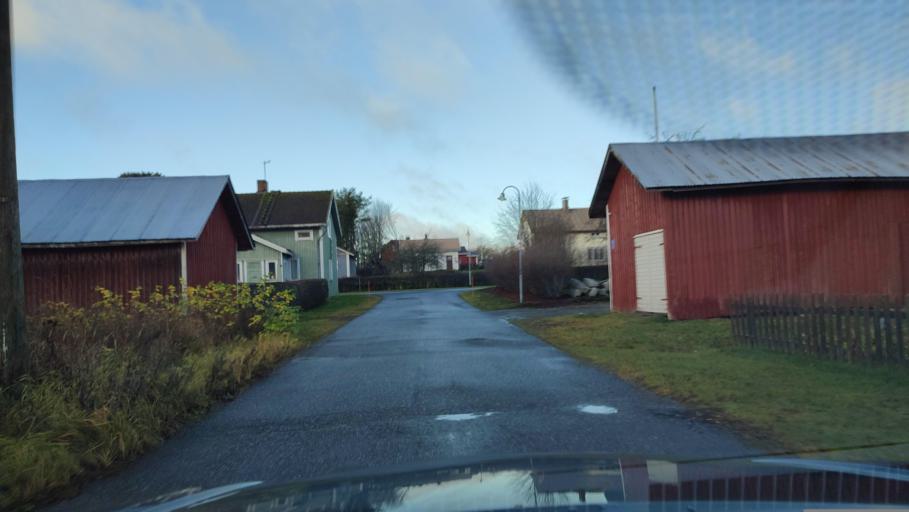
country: FI
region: Ostrobothnia
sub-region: Sydosterbotten
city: Kristinestad
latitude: 62.2671
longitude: 21.3736
